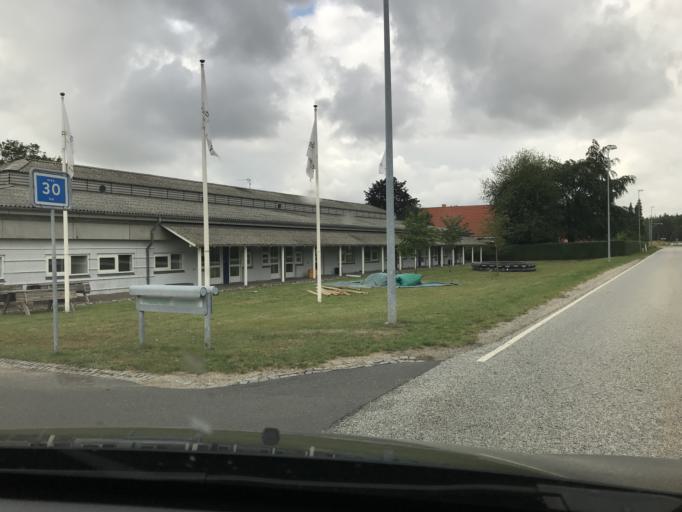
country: DK
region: Central Jutland
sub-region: Norddjurs Kommune
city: Auning
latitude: 56.3991
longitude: 10.4090
